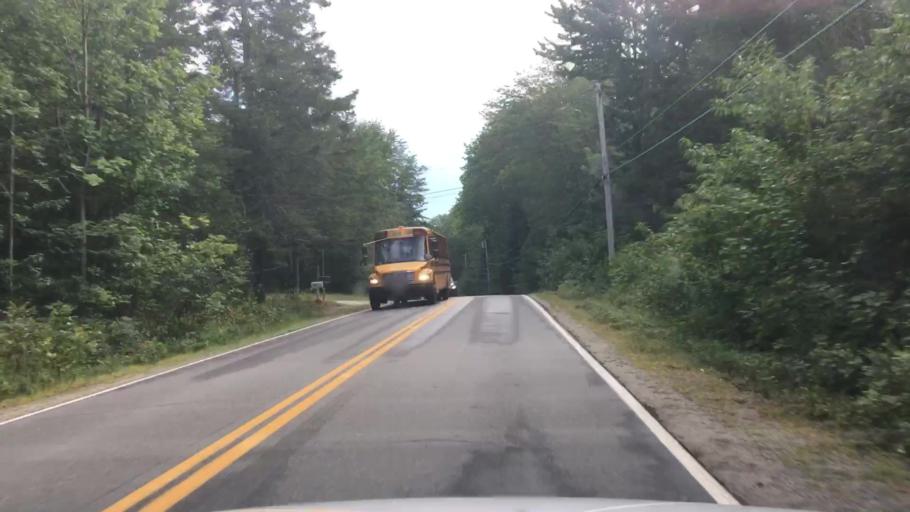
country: US
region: Maine
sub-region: Hancock County
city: Trenton
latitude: 44.4595
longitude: -68.4247
